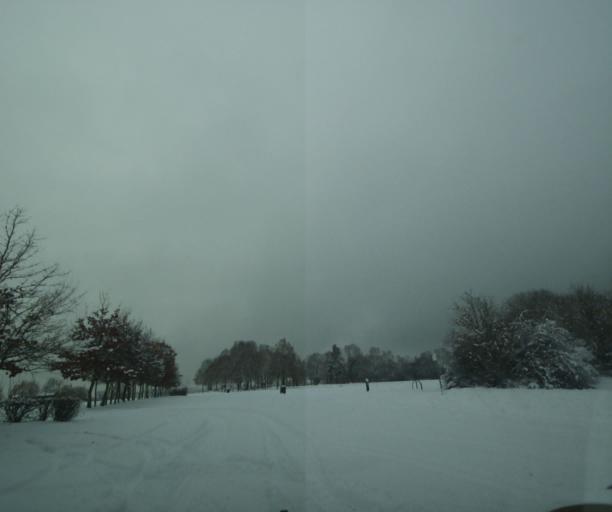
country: FR
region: Champagne-Ardenne
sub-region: Departement de la Haute-Marne
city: Montier-en-Der
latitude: 48.5575
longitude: 4.7904
